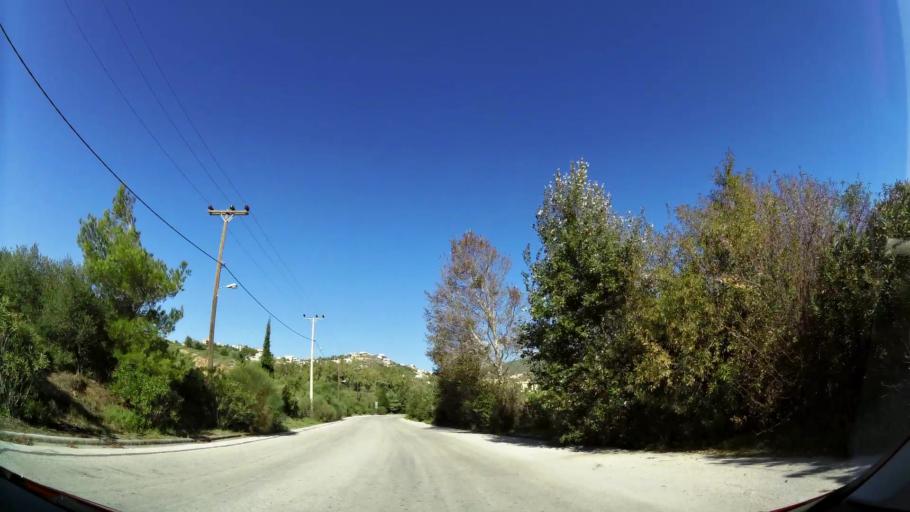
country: GR
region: Attica
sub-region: Nomarchia Anatolikis Attikis
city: Dhrafi
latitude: 38.0308
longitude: 23.9064
